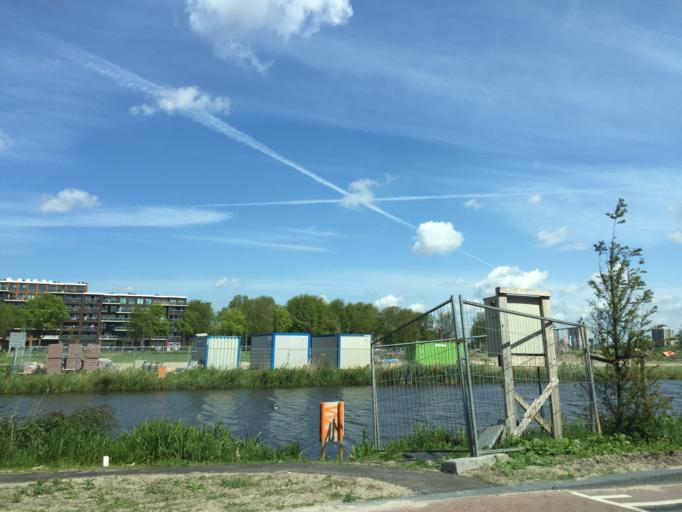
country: NL
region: North Holland
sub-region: Gemeente Haarlem
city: Haarlem
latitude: 52.3686
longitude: 4.6520
